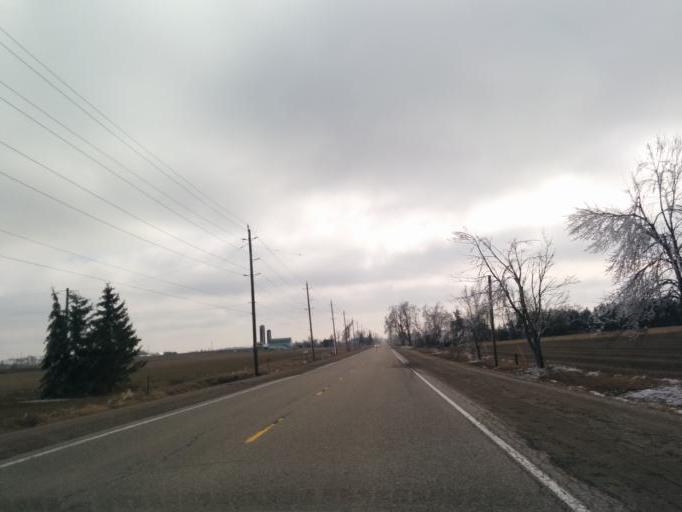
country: CA
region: Ontario
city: Waterloo
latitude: 43.6281
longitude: -80.5509
